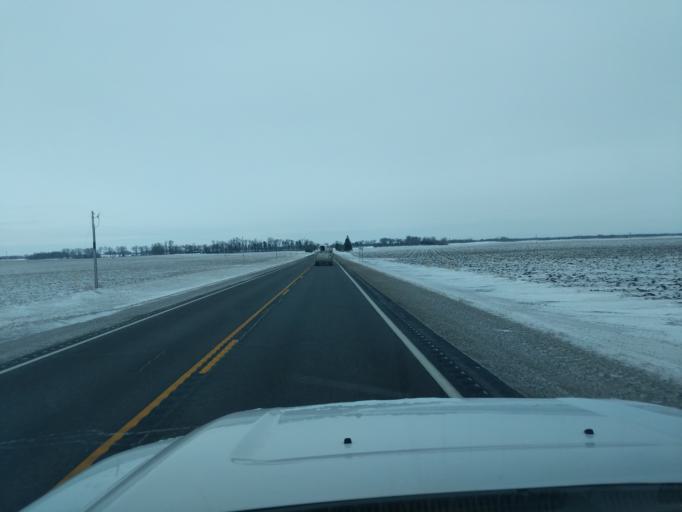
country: US
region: Minnesota
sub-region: Redwood County
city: Redwood Falls
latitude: 44.5971
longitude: -94.9944
